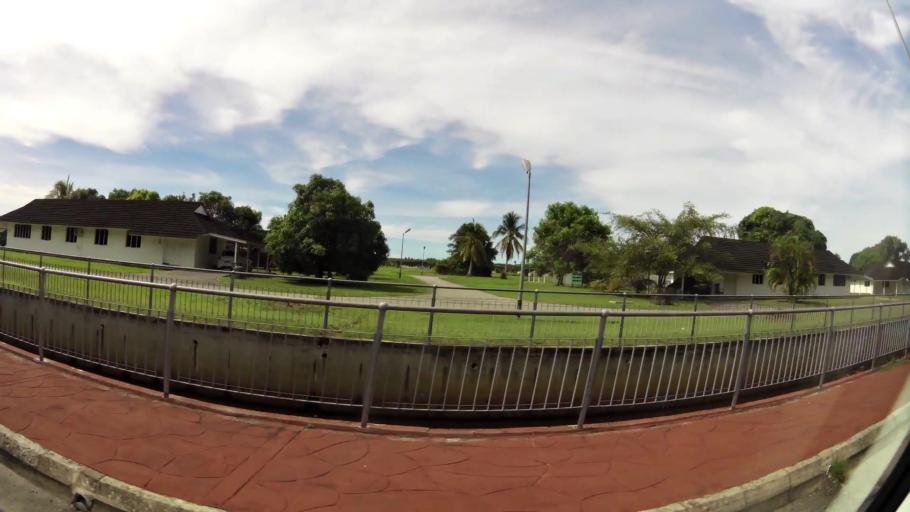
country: BN
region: Belait
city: Seria
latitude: 4.6125
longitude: 114.3204
